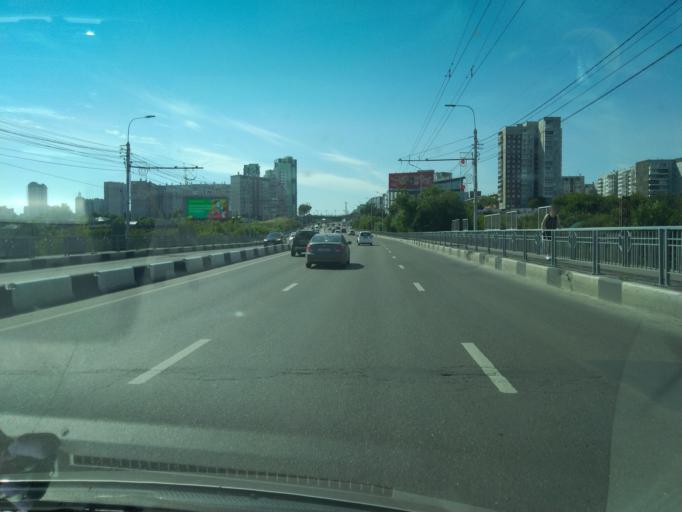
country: RU
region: Krasnoyarskiy
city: Krasnoyarsk
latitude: 56.0126
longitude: 92.8307
